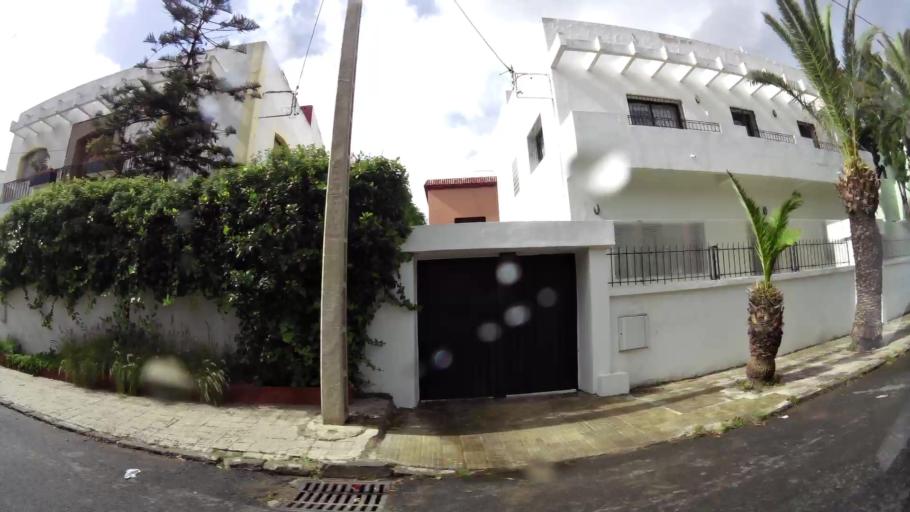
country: MA
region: Grand Casablanca
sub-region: Casablanca
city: Casablanca
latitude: 33.5558
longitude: -7.6069
